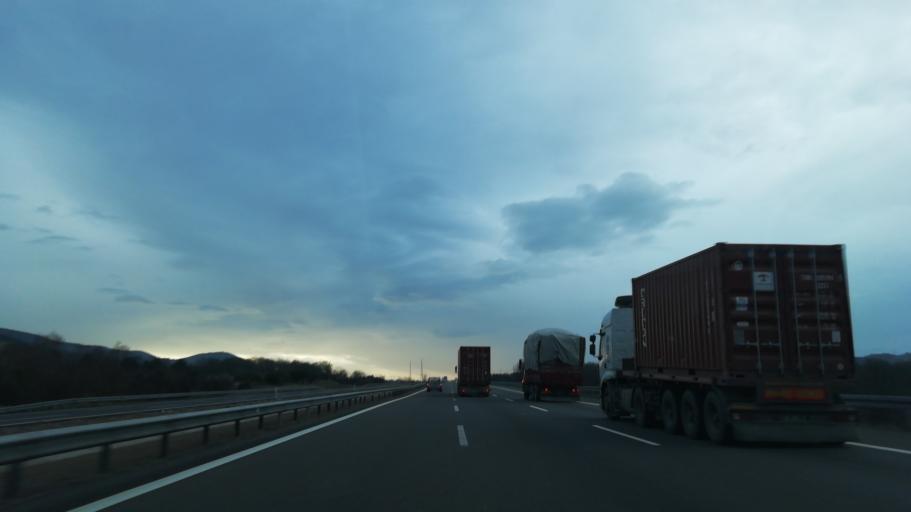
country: TR
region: Bolu
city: Yenicaga
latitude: 40.7535
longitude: 31.9551
